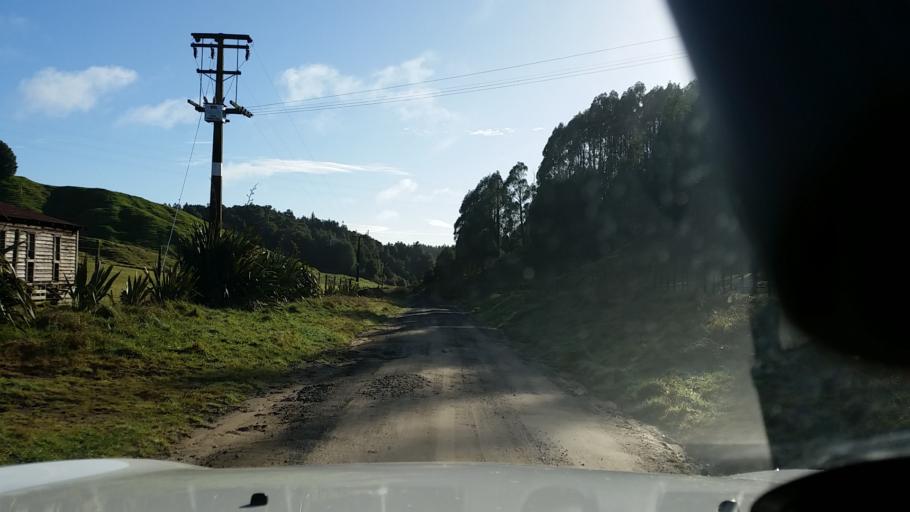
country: NZ
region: Bay of Plenty
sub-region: Kawerau District
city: Kawerau
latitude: -38.0142
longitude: 176.5972
